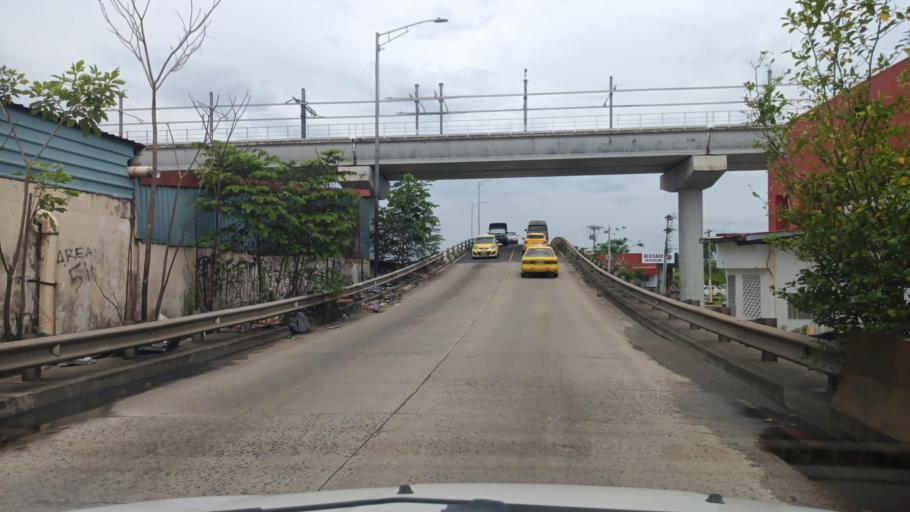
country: PA
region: Panama
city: San Miguelito
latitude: 9.0612
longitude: -79.4270
